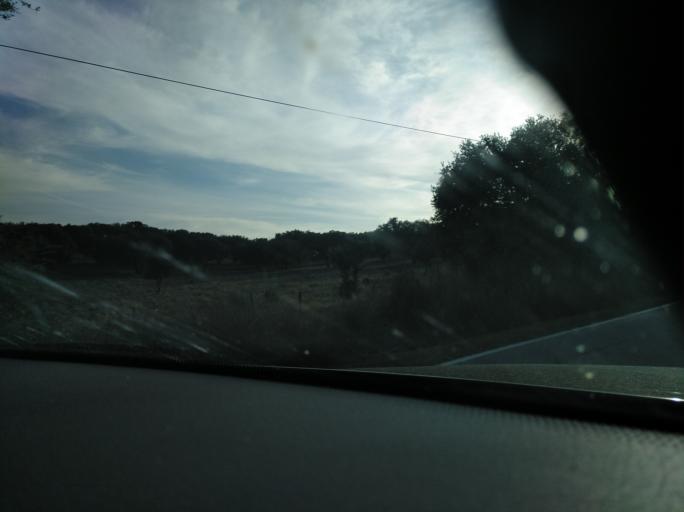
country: PT
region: Portalegre
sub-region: Fronteira
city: Fronteira
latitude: 38.9591
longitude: -7.6188
